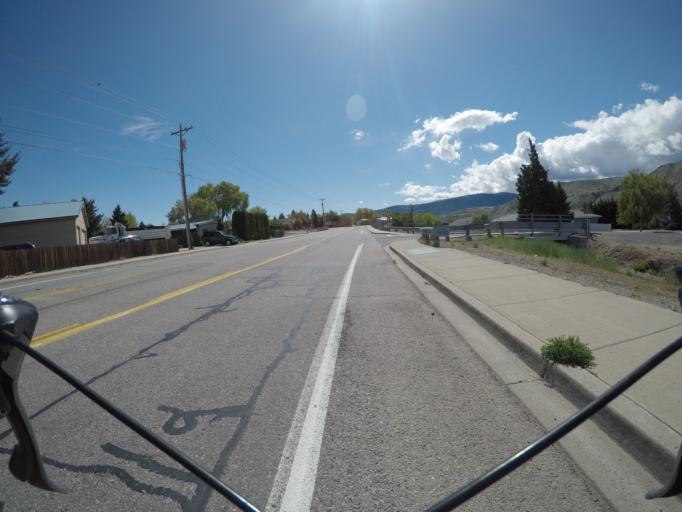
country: US
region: Washington
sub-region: Chelan County
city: South Wenatchee
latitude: 47.3996
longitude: -120.2756
